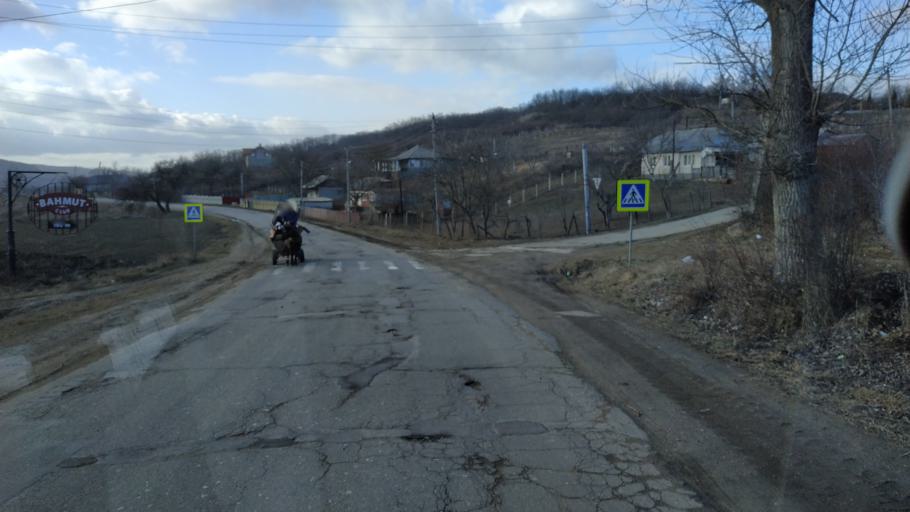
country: MD
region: Calarasi
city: Calarasi
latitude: 47.3302
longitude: 28.0894
